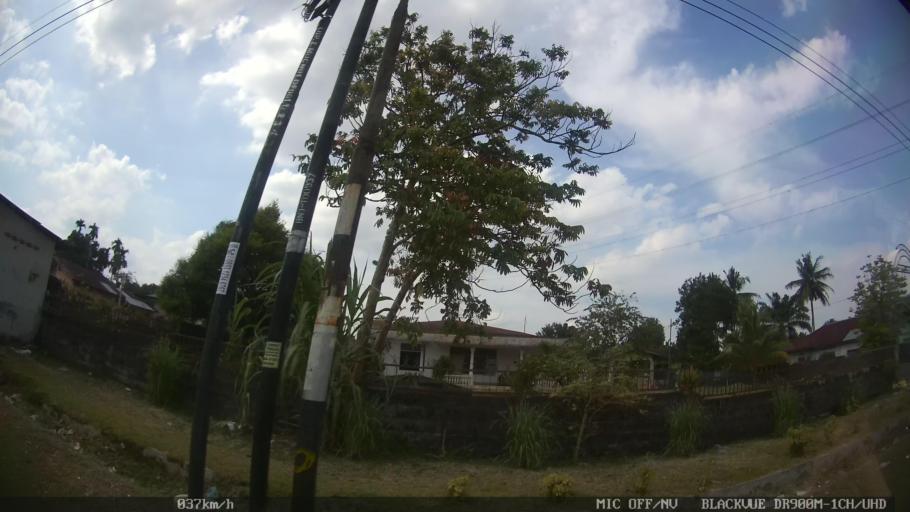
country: ID
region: North Sumatra
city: Binjai
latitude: 3.6131
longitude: 98.5048
